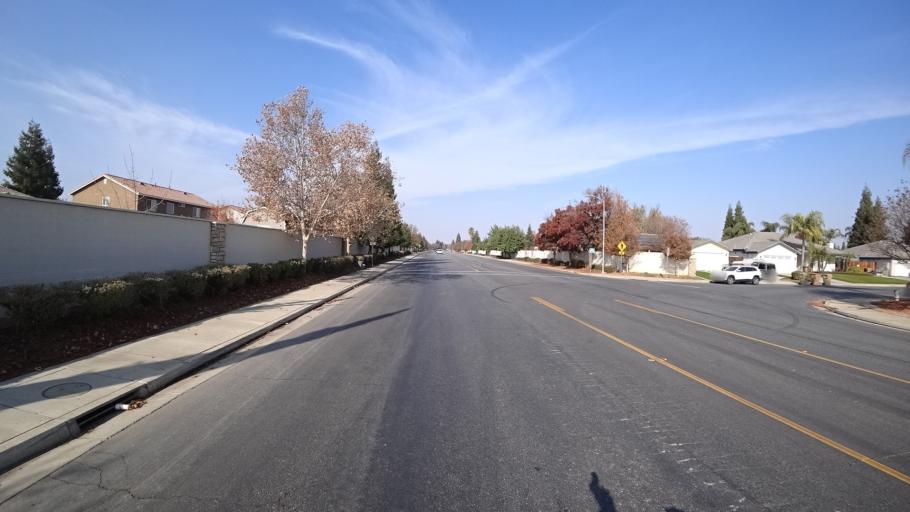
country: US
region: California
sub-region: Kern County
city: Greenacres
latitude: 35.4218
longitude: -119.1166
